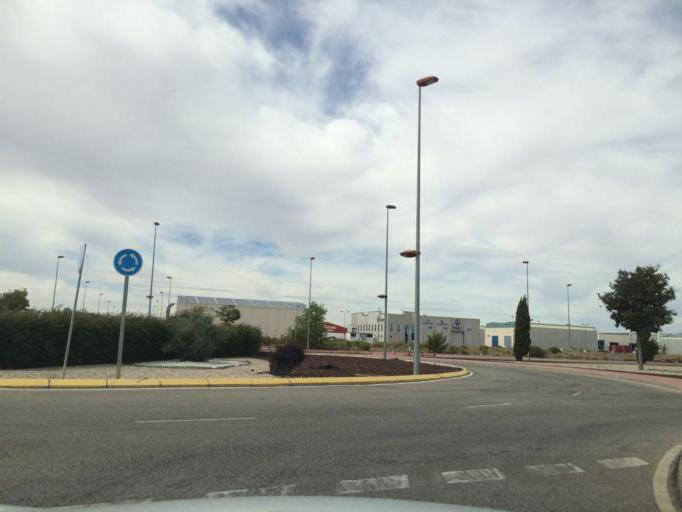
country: ES
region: Castille-La Mancha
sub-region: Provincia de Albacete
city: Albacete
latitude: 39.0262
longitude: -1.8869
